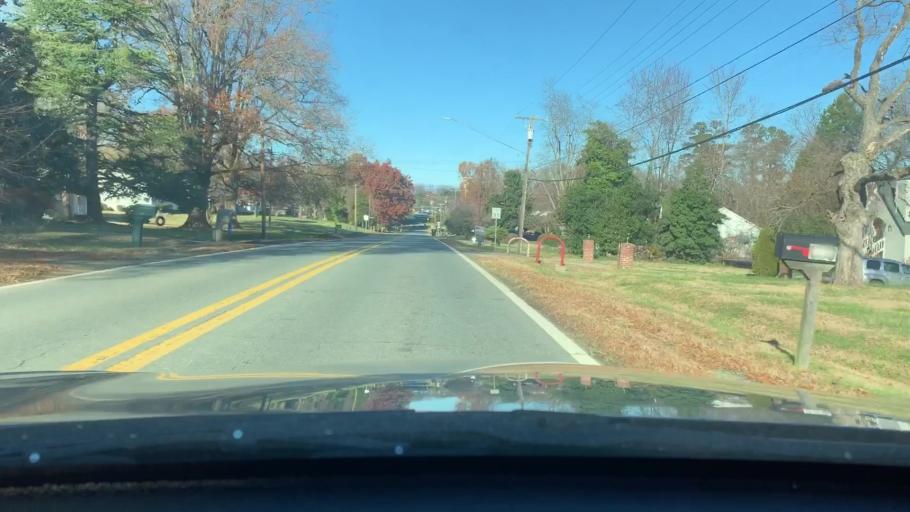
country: US
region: North Carolina
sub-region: Alamance County
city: Burlington
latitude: 36.0795
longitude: -79.4549
